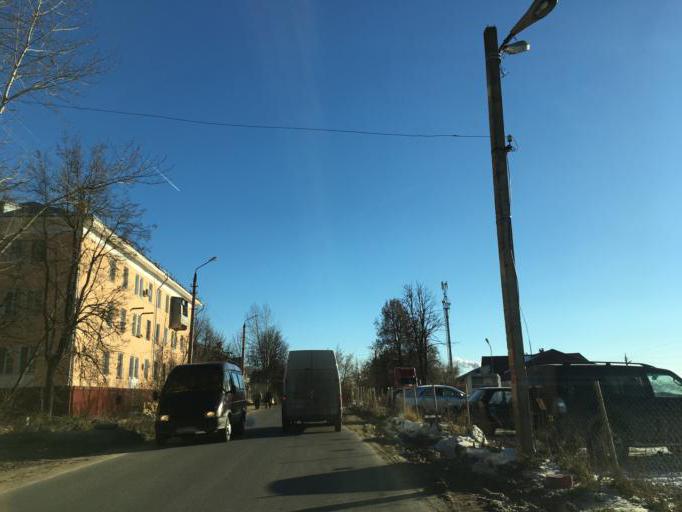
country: RU
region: Tula
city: Tula
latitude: 54.1838
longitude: 37.6936
